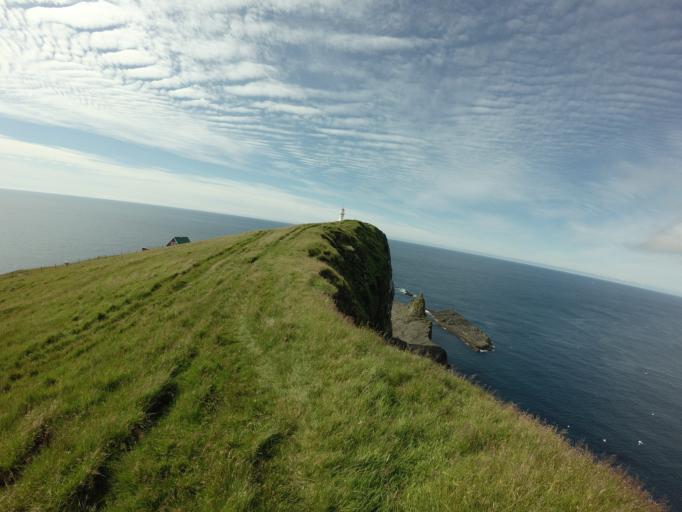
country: FO
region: Vagar
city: Sorvagur
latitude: 62.0983
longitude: -7.6789
